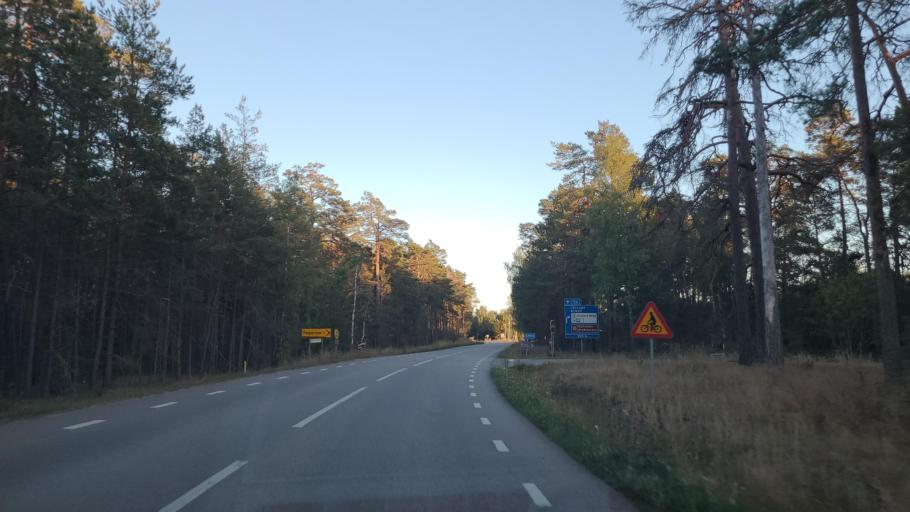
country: SE
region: Kalmar
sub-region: Borgholms Kommun
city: Borgholm
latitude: 57.2638
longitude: 17.0313
